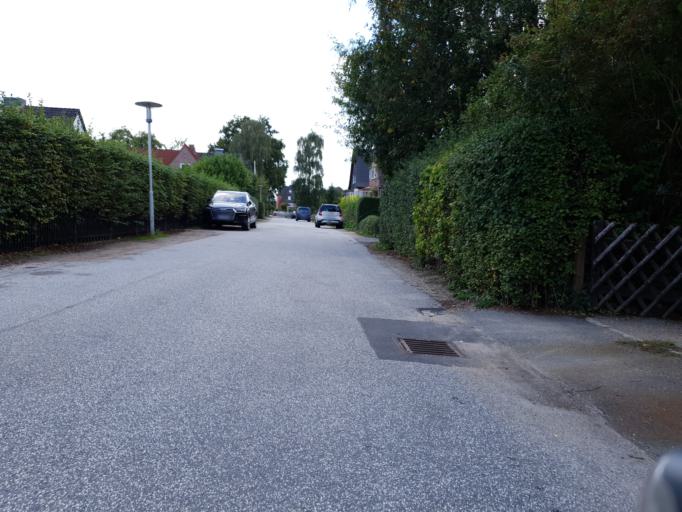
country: DE
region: Schleswig-Holstein
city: Kronshagen
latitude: 54.3312
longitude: 10.0952
